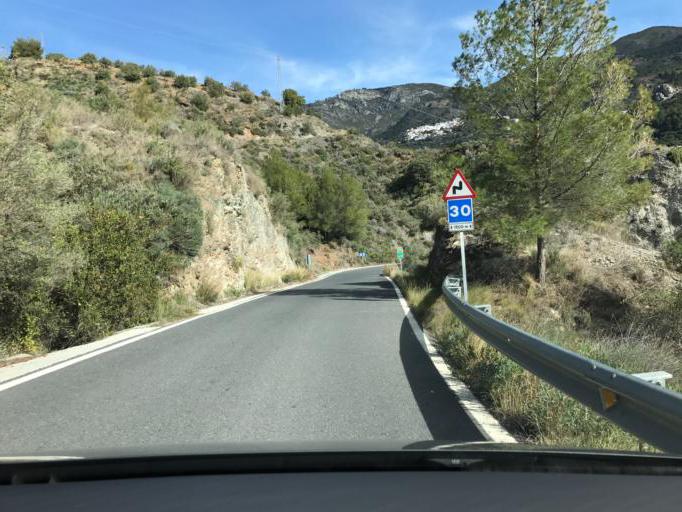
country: ES
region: Andalusia
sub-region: Provincia de Granada
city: Otivar
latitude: 36.8265
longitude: -3.6888
